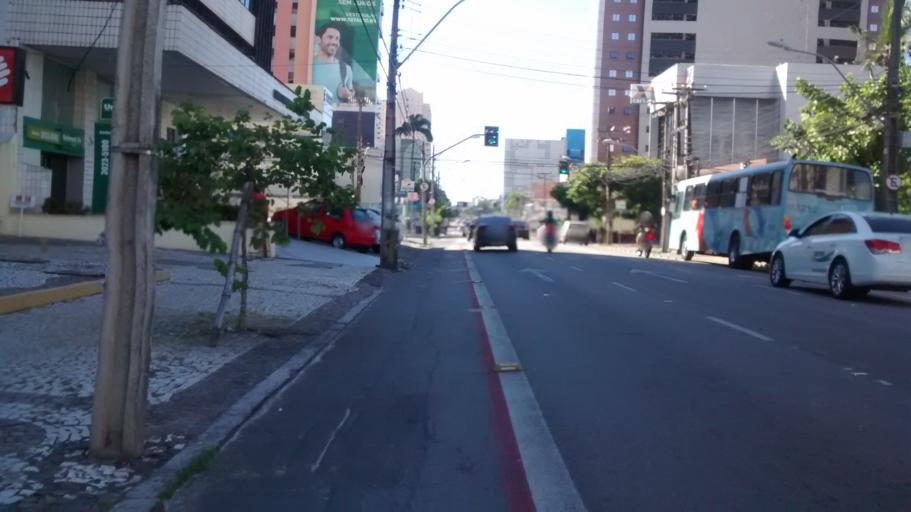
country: BR
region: Ceara
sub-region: Fortaleza
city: Fortaleza
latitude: -3.7354
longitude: -38.5008
